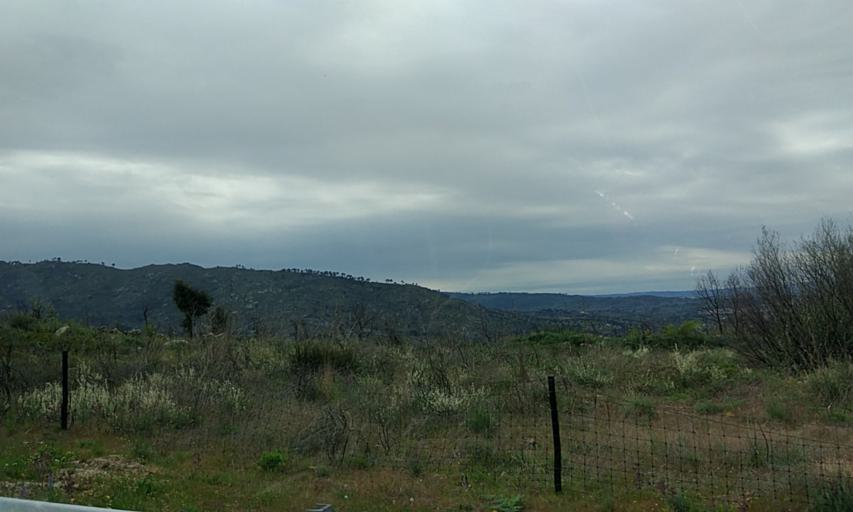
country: PT
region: Guarda
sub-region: Guarda
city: Guarda
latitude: 40.6150
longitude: -7.2824
